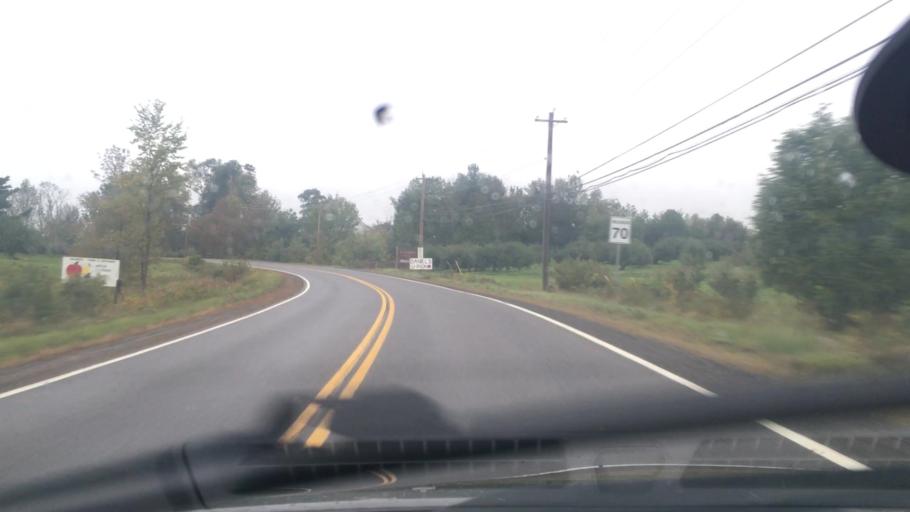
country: CA
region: Nova Scotia
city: Windsor
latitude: 44.9503
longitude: -64.1733
